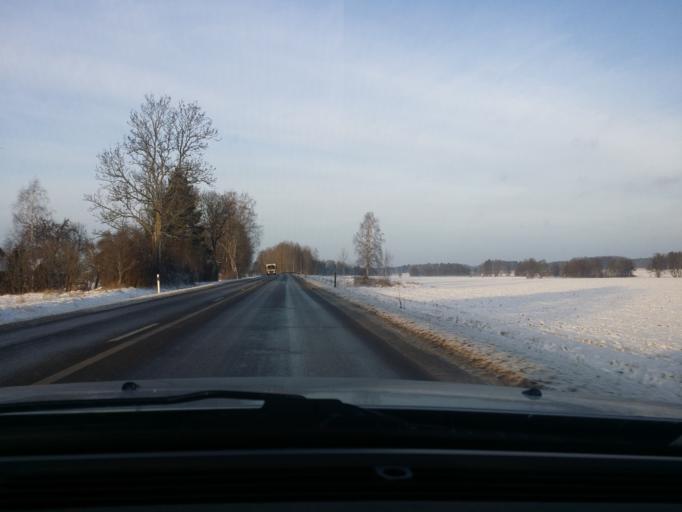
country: SE
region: OErebro
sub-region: Lindesbergs Kommun
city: Fellingsbro
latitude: 59.4649
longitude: 15.5577
